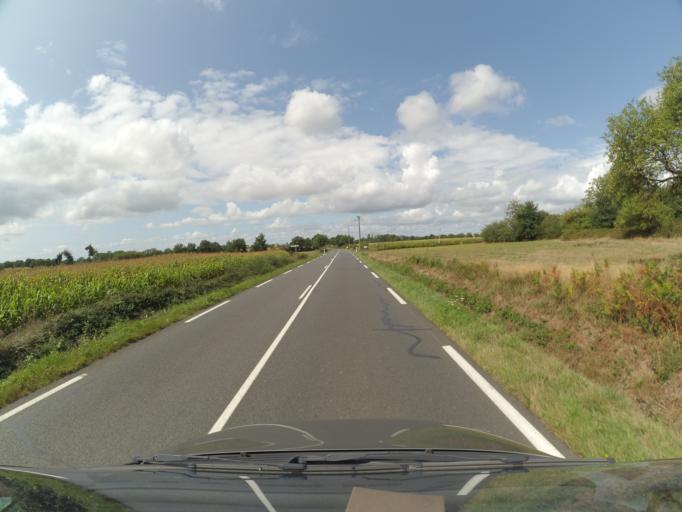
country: FR
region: Pays de la Loire
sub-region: Departement de la Vendee
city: La Bruffiere
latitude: 47.0319
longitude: -1.2075
